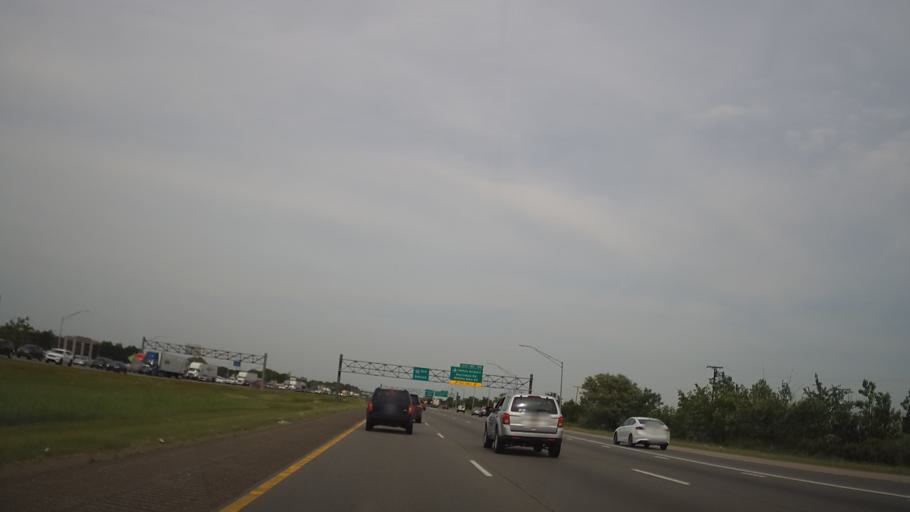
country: US
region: Michigan
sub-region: Wayne County
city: Romulus
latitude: 42.2360
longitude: -83.3534
